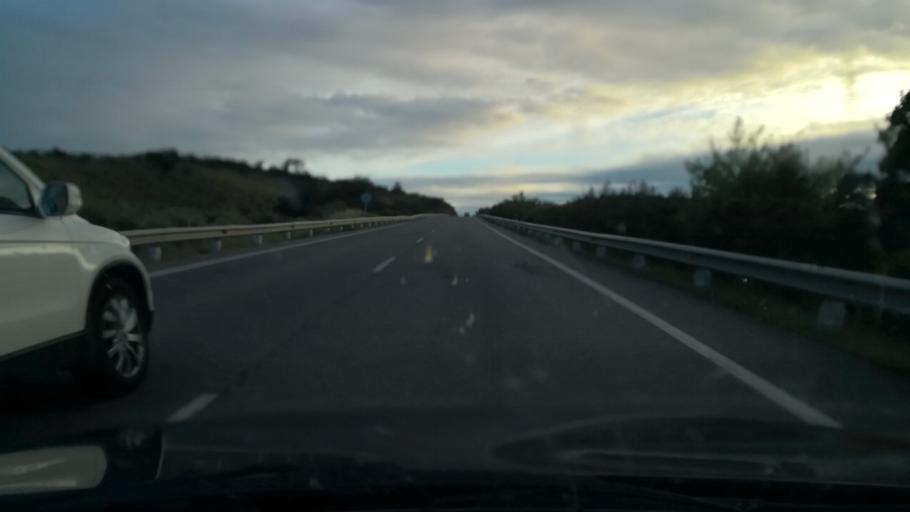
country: ES
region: Extremadura
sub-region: Provincia de Badajoz
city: Puebla de Obando
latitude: 39.1699
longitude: -6.6284
